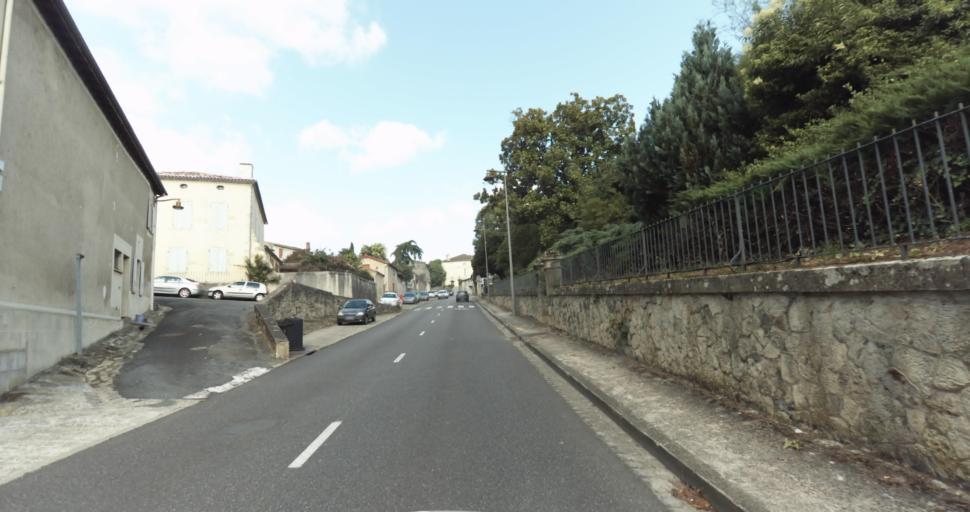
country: FR
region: Aquitaine
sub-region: Departement de la Gironde
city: Bazas
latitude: 44.4327
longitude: -0.2111
